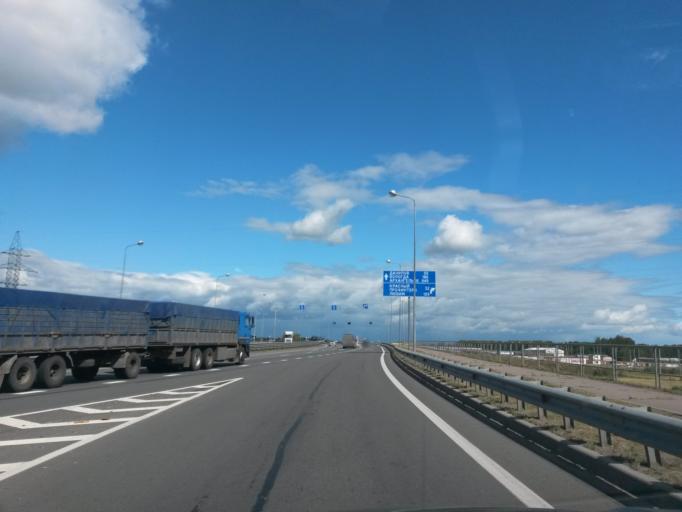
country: RU
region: Jaroslavl
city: Yaroslavl
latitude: 57.6830
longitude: 39.8998
